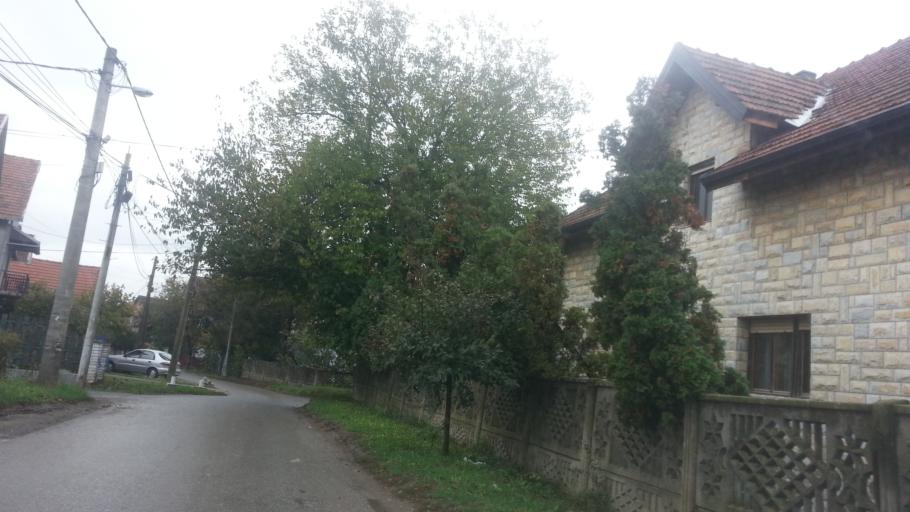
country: RS
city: Novi Banovci
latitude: 44.9119
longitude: 20.2851
